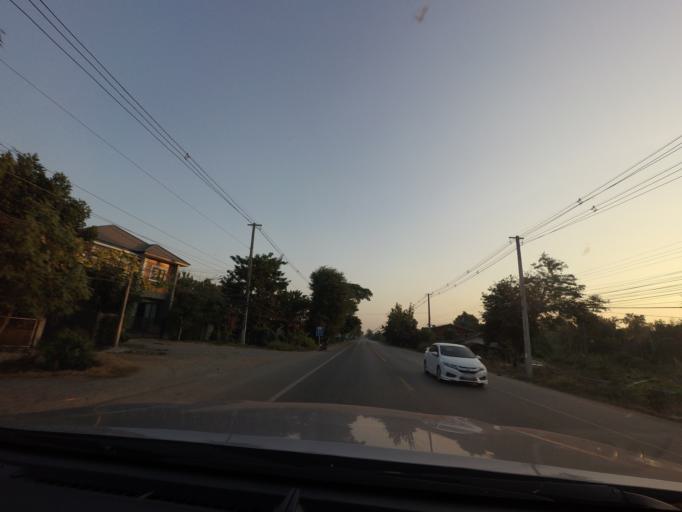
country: TH
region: Sukhothai
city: Si Samrong
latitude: 17.1257
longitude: 99.8507
